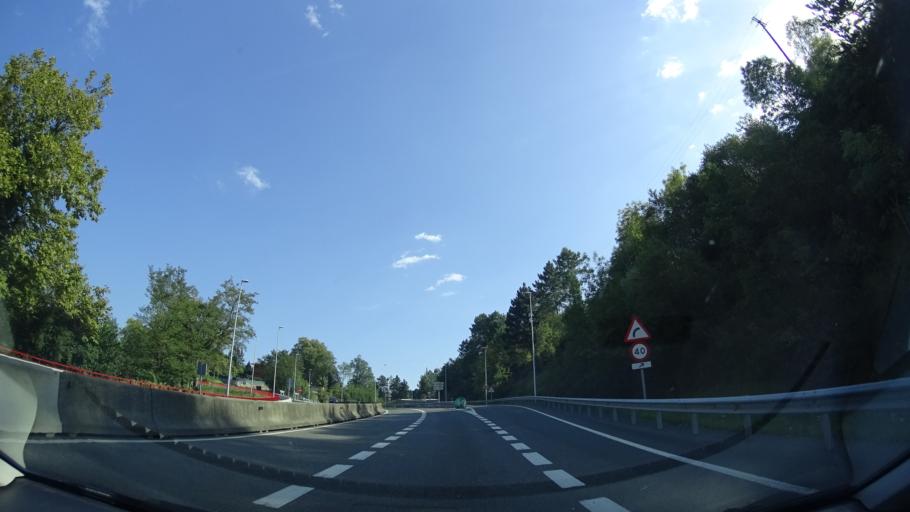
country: ES
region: Basque Country
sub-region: Bizkaia
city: Santutxu
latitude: 43.2683
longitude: -2.9072
